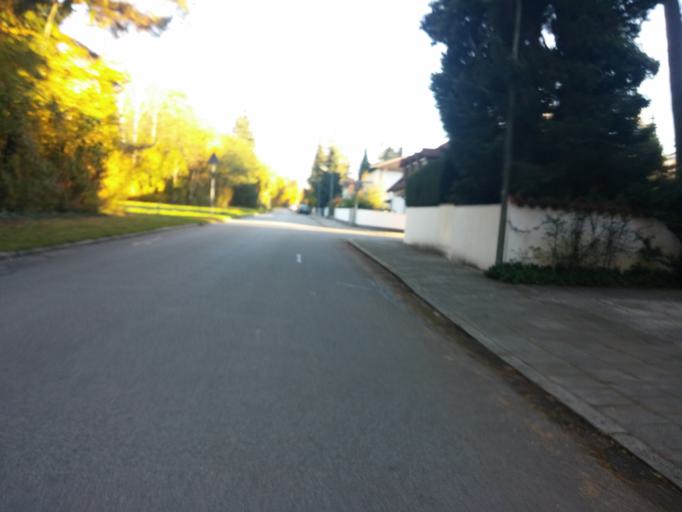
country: DE
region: Bavaria
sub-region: Upper Bavaria
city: Haar
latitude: 48.1054
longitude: 11.7020
